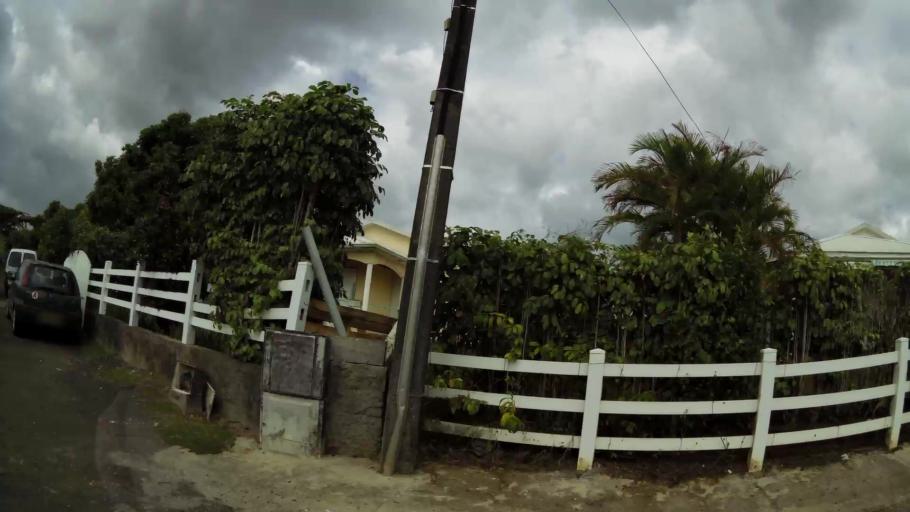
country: GP
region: Guadeloupe
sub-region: Guadeloupe
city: Baie-Mahault
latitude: 16.2568
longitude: -61.5774
